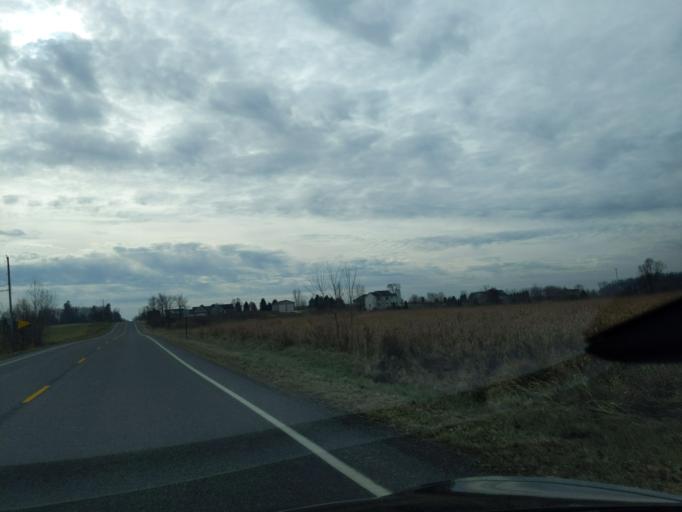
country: US
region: Michigan
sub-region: Ingham County
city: Mason
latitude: 42.5368
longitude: -84.5225
